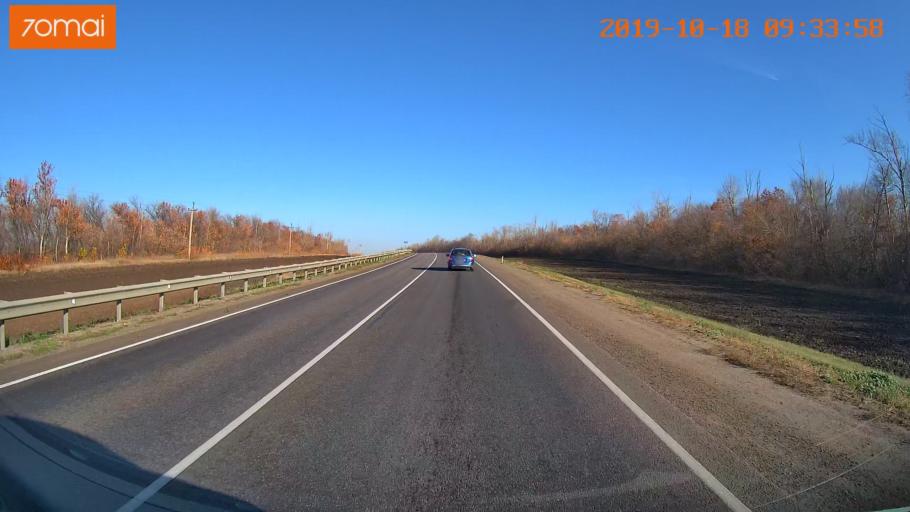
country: RU
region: Tula
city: Yefremov
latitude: 53.1740
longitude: 38.1526
